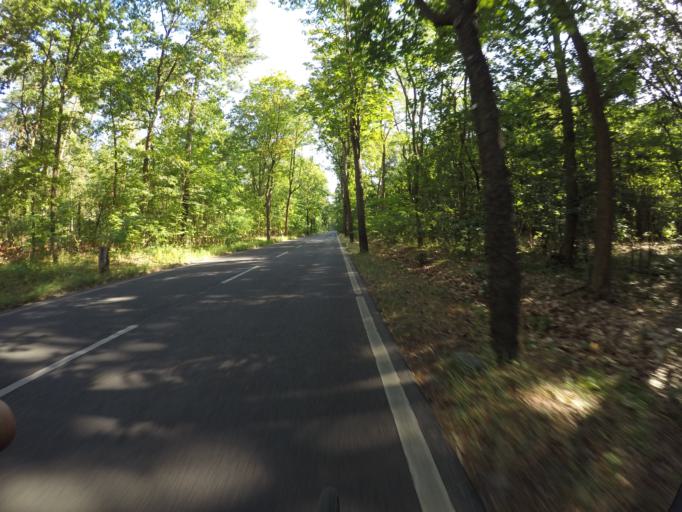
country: DE
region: Berlin
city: Schmockwitz
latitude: 52.3687
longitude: 13.6564
